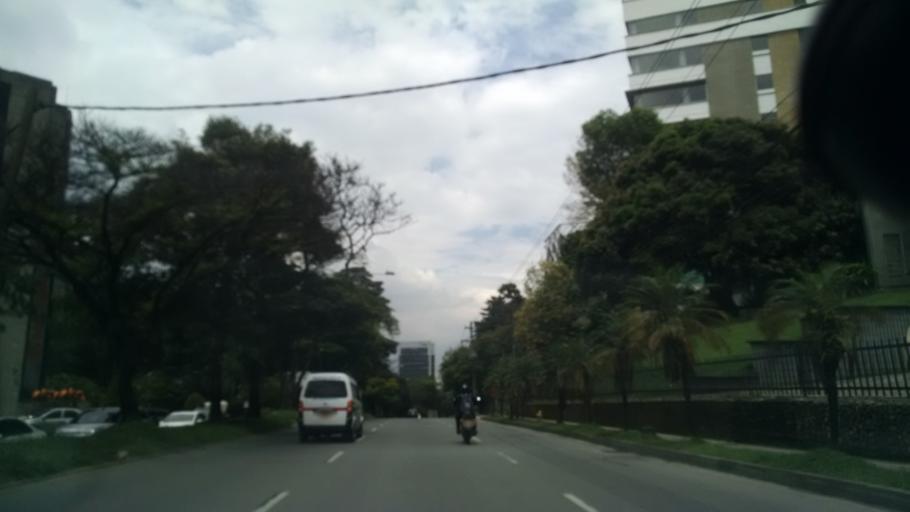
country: CO
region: Antioquia
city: Medellin
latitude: 6.2154
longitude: -75.5699
